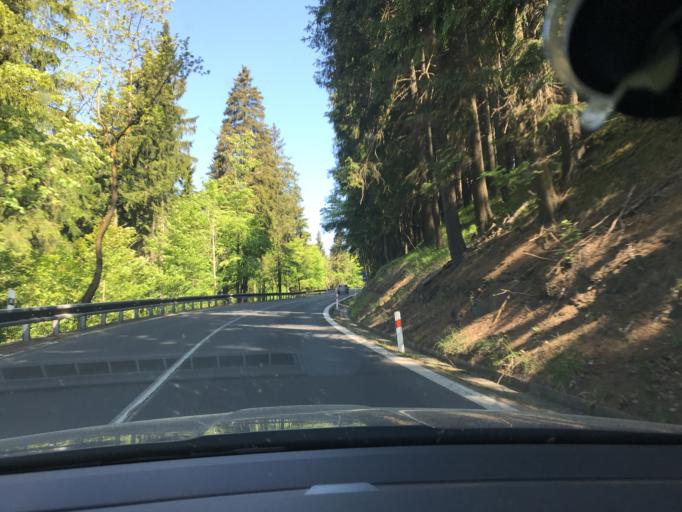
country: CZ
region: Karlovarsky
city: Jachymov
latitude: 50.3797
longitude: 12.9102
